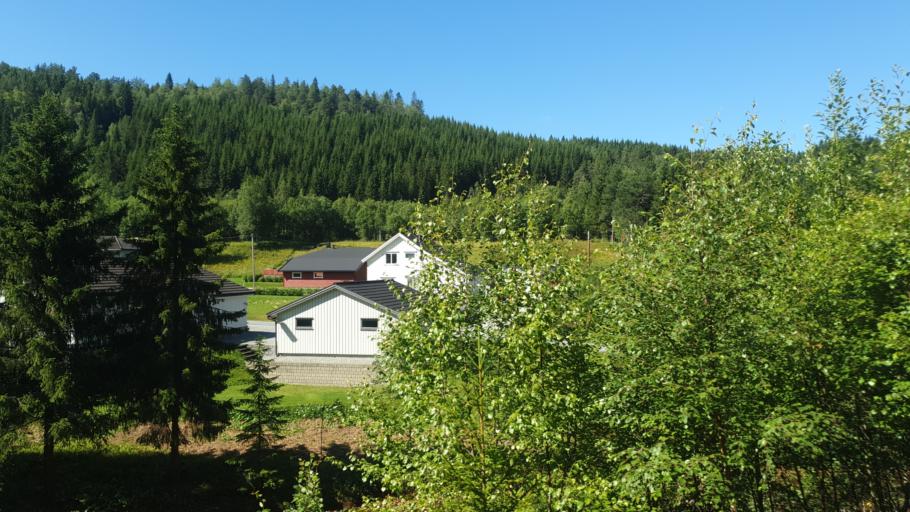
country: NO
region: Sor-Trondelag
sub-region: Meldal
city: Meldal
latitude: 63.1363
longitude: 9.7107
